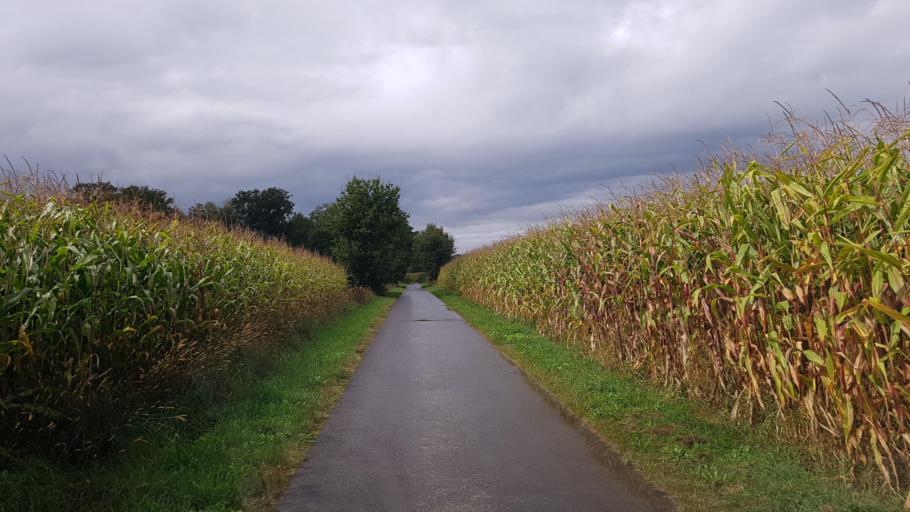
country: DE
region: Brandenburg
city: Tettau
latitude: 51.4620
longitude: 13.7195
